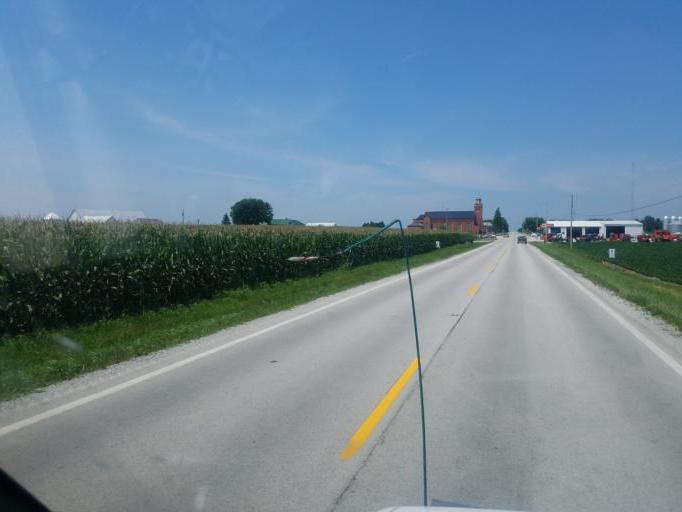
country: US
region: Ohio
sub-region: Auglaize County
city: Minster
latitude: 40.3823
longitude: -84.4340
